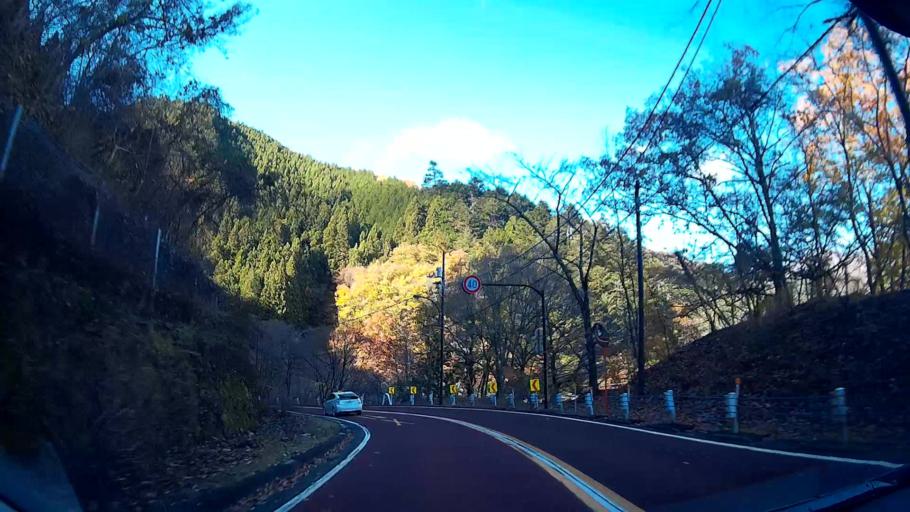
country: JP
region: Yamanashi
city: Uenohara
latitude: 35.7721
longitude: 139.0188
